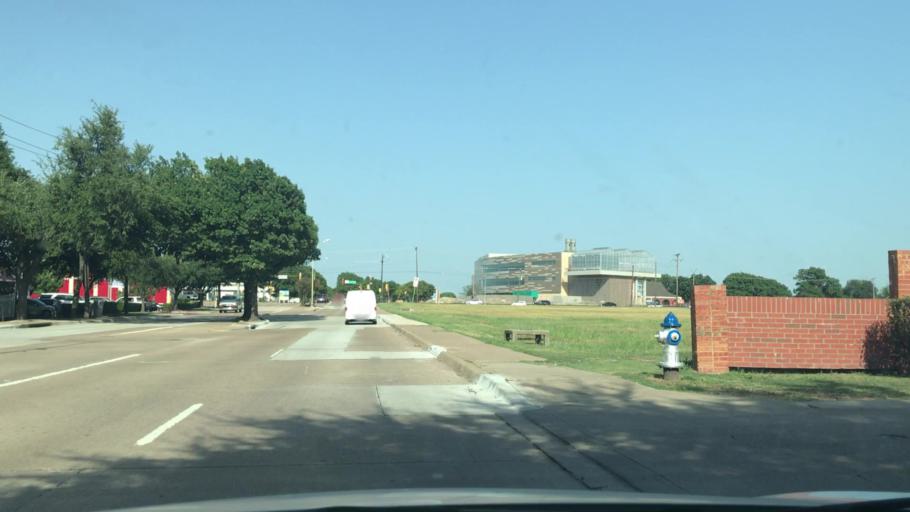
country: US
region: Texas
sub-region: Dallas County
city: Richardson
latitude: 32.9879
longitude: -96.7705
